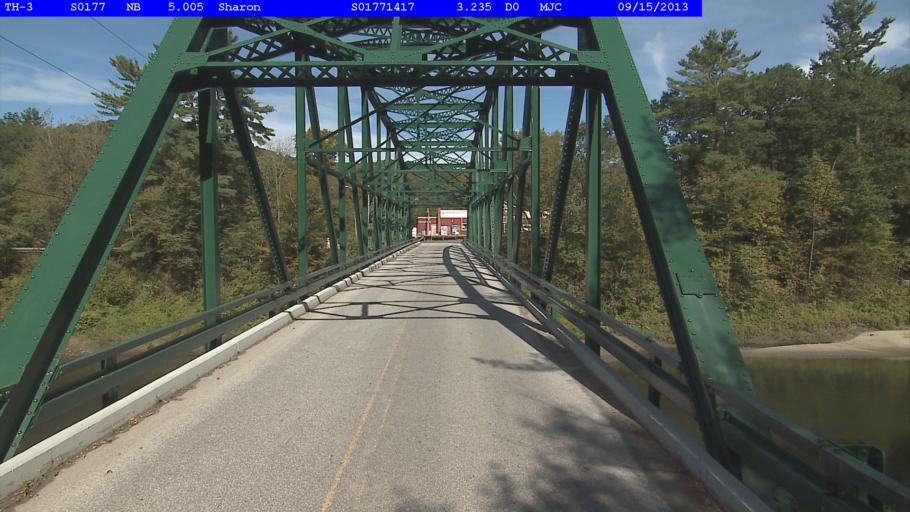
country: US
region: Vermont
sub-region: Windsor County
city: Woodstock
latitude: 43.7820
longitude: -72.4594
